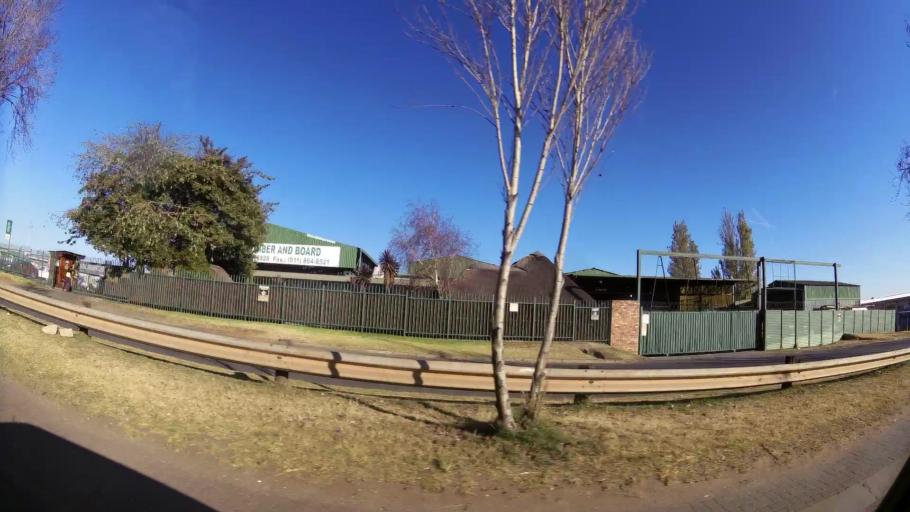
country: ZA
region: Gauteng
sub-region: Ekurhuleni Metropolitan Municipality
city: Germiston
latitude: -26.2952
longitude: 28.1376
